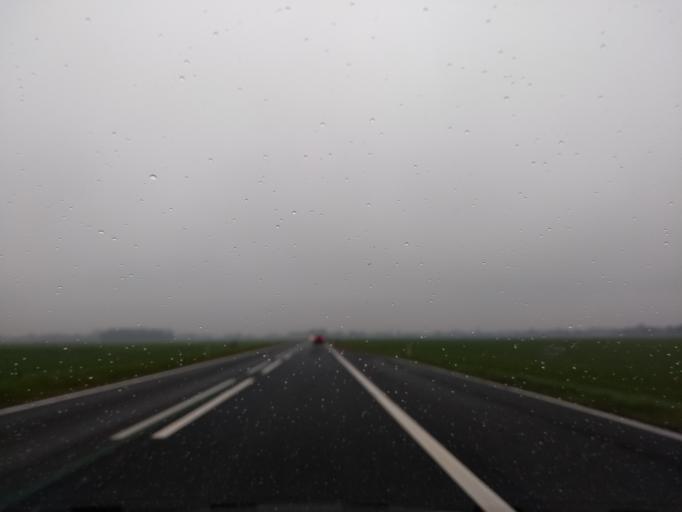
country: NL
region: Overijssel
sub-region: Gemeente Twenterand
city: Westerhaar-Vriezenveensewijk
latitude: 52.4892
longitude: 6.5984
